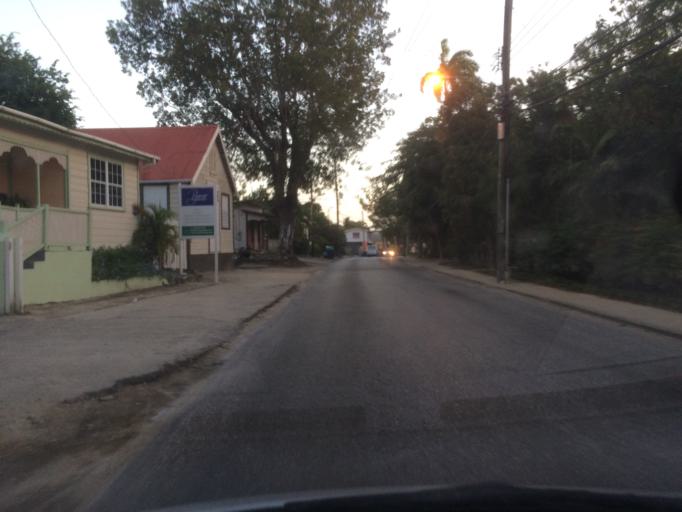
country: BB
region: Saint James
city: Holetown
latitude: 13.2112
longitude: -59.6395
